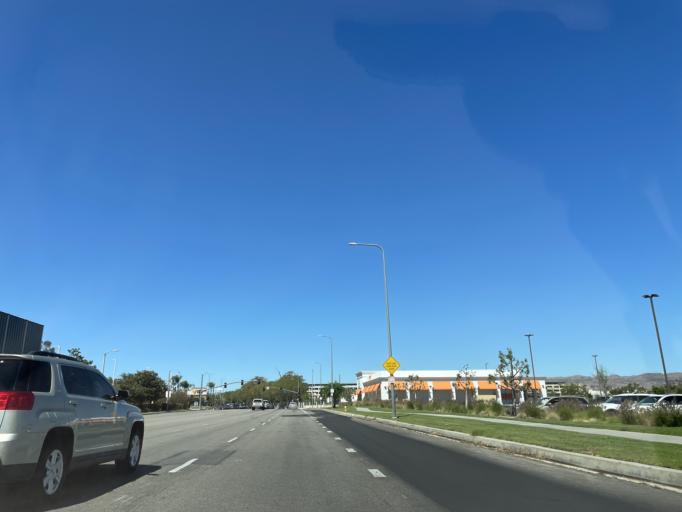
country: US
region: California
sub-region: Los Angeles County
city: Canoga Park
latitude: 34.1884
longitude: -118.5955
